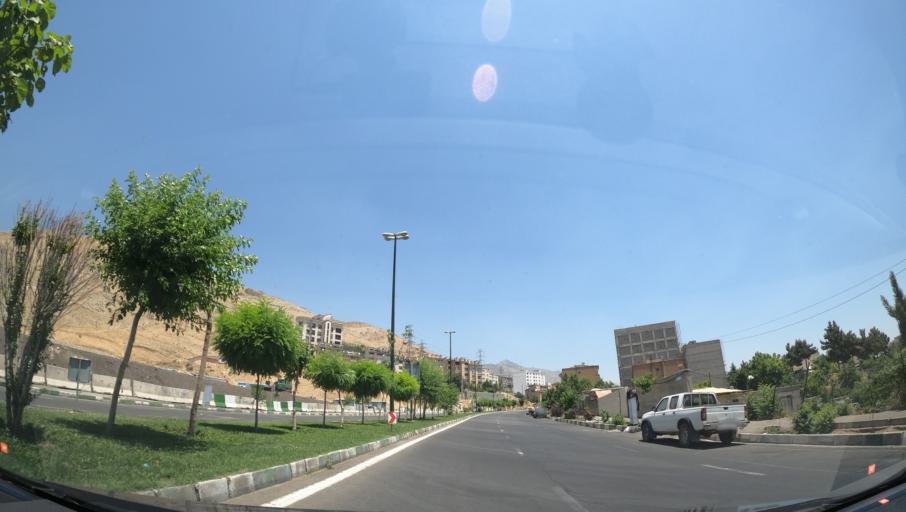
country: IR
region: Tehran
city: Tajrish
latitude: 35.8096
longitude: 51.3897
